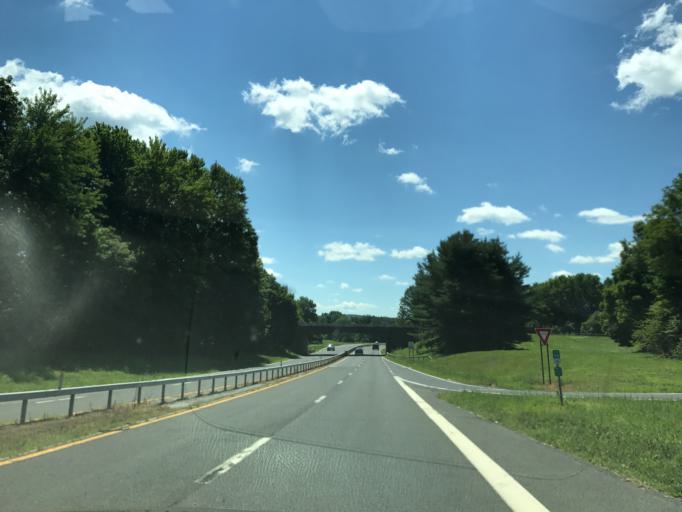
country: US
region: New York
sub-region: Dutchess County
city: Millbrook
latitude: 41.8263
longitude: -73.7733
